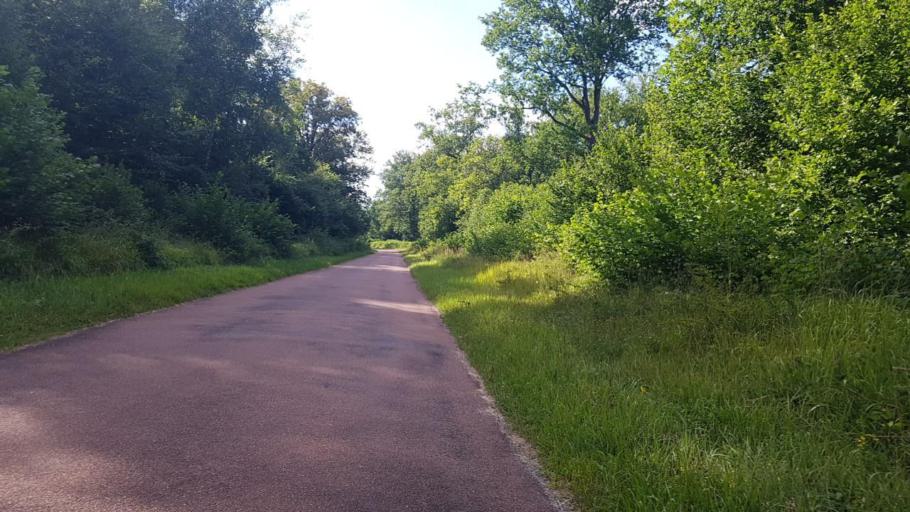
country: FR
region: Picardie
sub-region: Departement de l'Oise
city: Chamant
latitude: 49.1771
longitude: 2.6227
